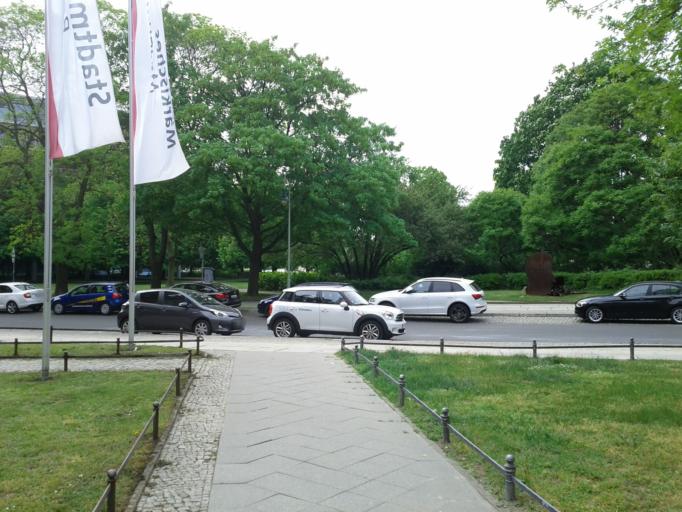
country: DE
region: Berlin
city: Berlin
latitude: 52.5140
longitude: 13.4153
